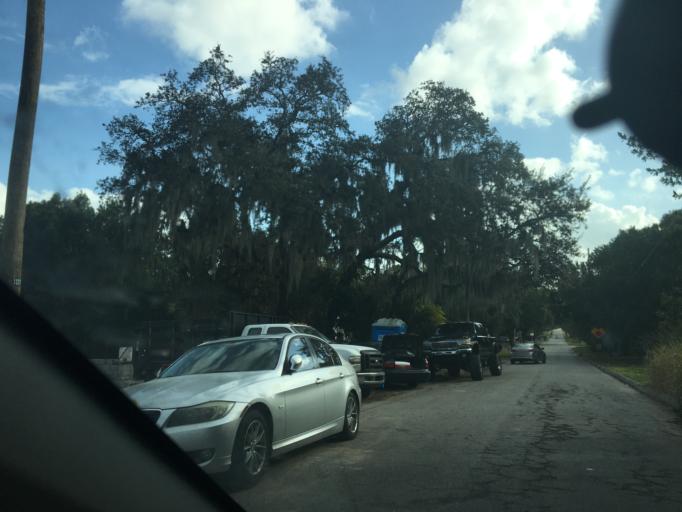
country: US
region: Florida
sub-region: Hillsborough County
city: Temple Terrace
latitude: 28.0302
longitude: -82.4182
